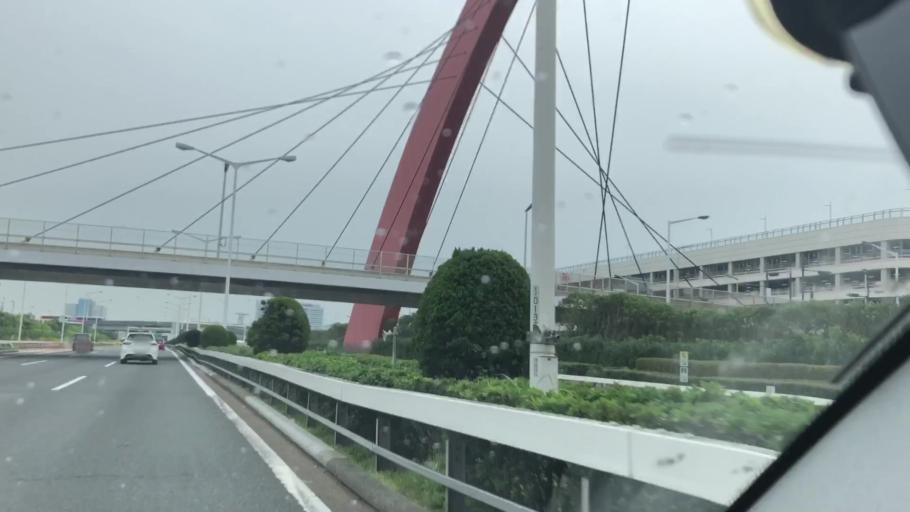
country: JP
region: Kanagawa
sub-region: Kawasaki-shi
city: Kawasaki
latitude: 35.5501
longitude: 139.7863
